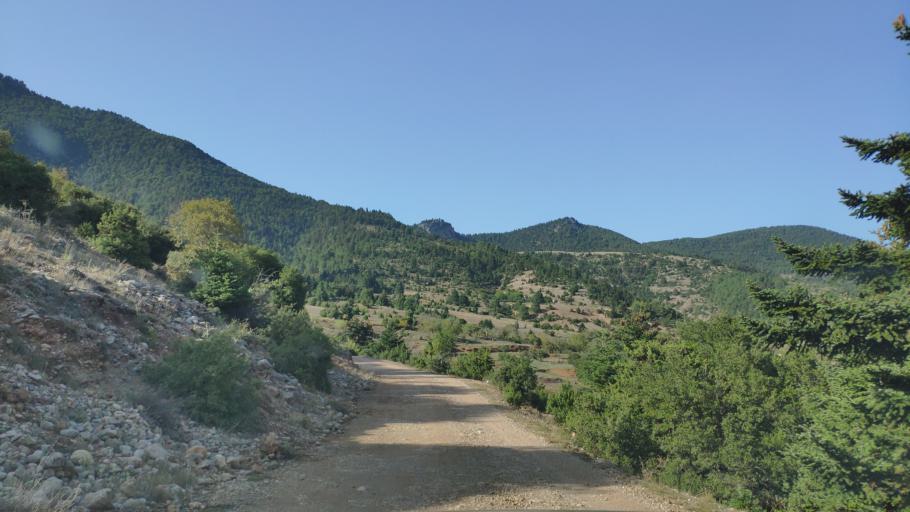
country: GR
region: West Greece
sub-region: Nomos Achaias
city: Aiyira
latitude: 37.9870
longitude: 22.3485
